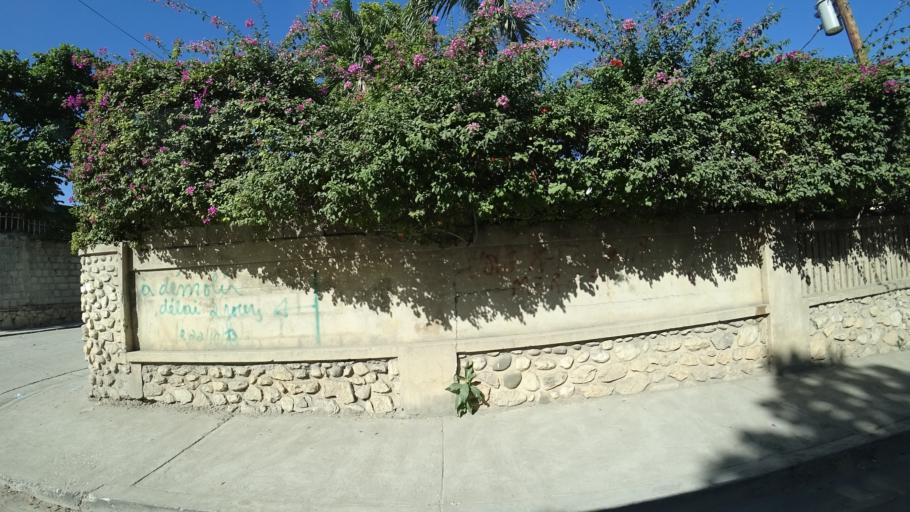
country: HT
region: Ouest
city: Delmas 73
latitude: 18.5563
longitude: -72.3069
